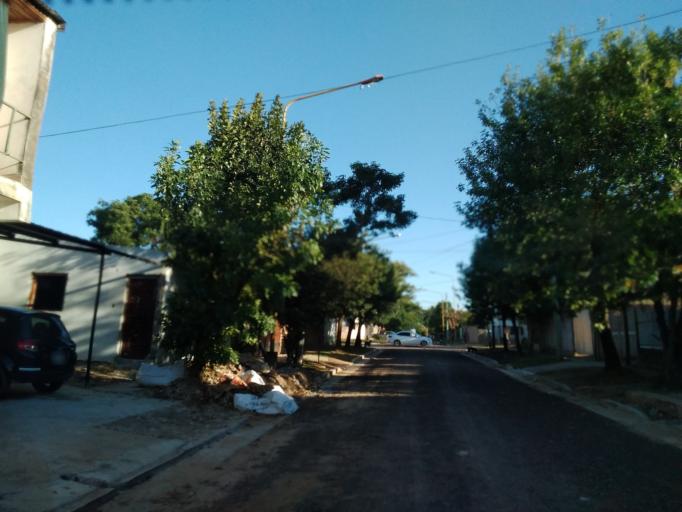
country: AR
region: Corrientes
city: Corrientes
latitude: -27.5054
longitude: -58.8002
